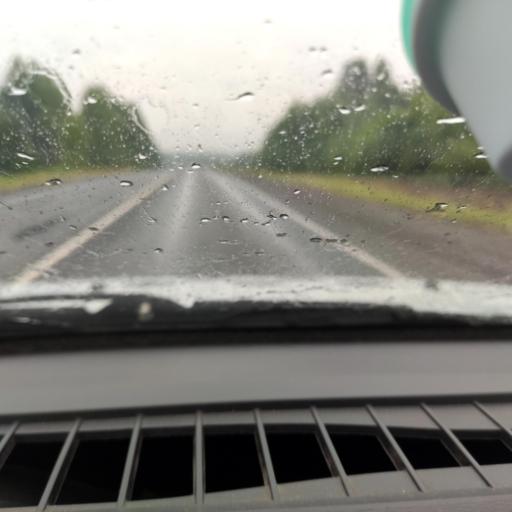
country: RU
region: Perm
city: Berezniki
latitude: 58.8752
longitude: 56.7627
